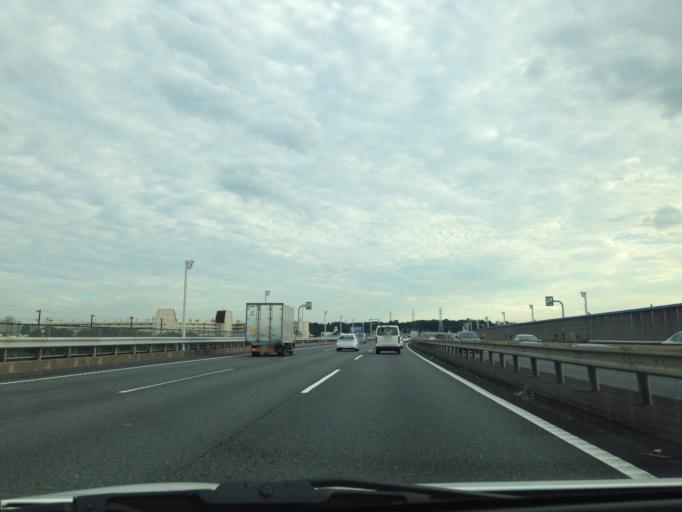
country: JP
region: Tokyo
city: Chofugaoka
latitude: 35.6200
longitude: 139.5972
